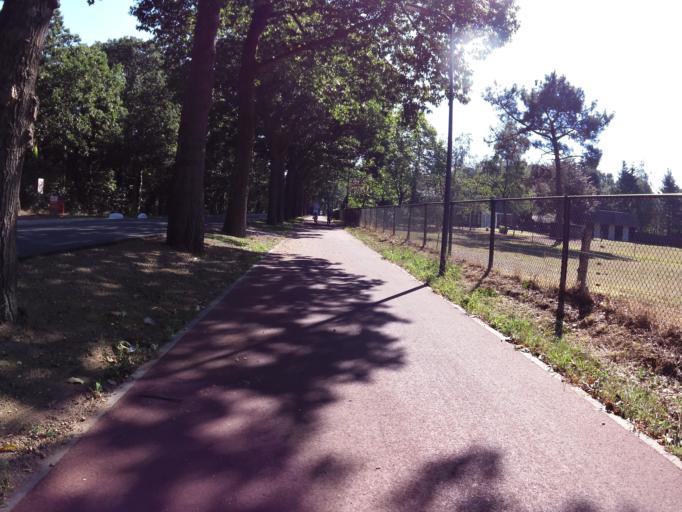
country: NL
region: North Brabant
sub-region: Gemeente Maasdonk
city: Geffen
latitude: 51.7224
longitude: 5.3980
